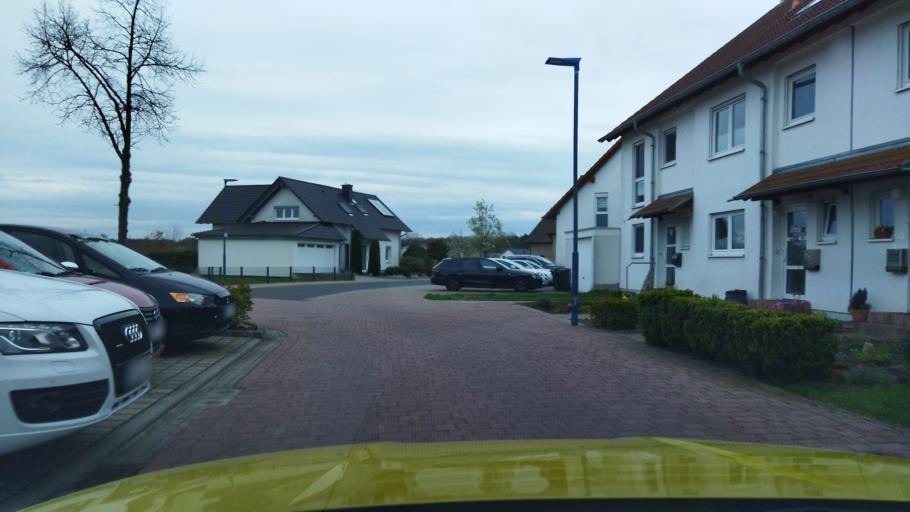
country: DE
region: Rheinland-Pfalz
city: Hanhofen
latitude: 49.3186
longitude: 8.3485
